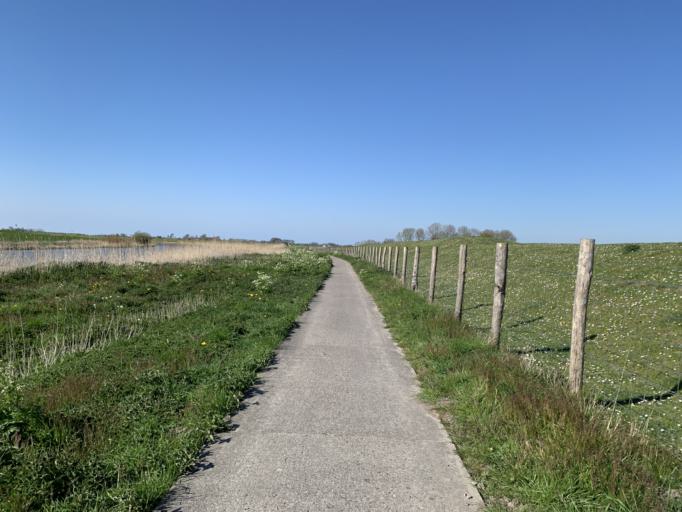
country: NL
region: Groningen
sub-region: Gemeente Winsum
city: Winsum
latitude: 53.2930
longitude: 6.5046
